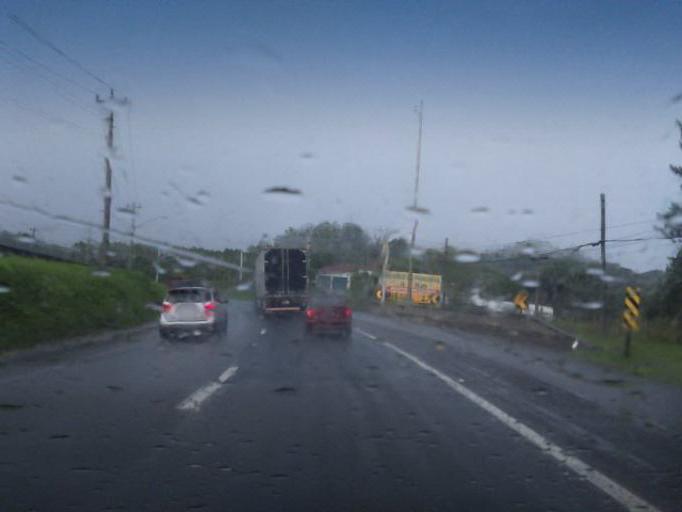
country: BR
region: Sao Paulo
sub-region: Sao Lourenco Da Serra
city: Sao Lourenco da Serra
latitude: -23.9149
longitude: -46.9890
